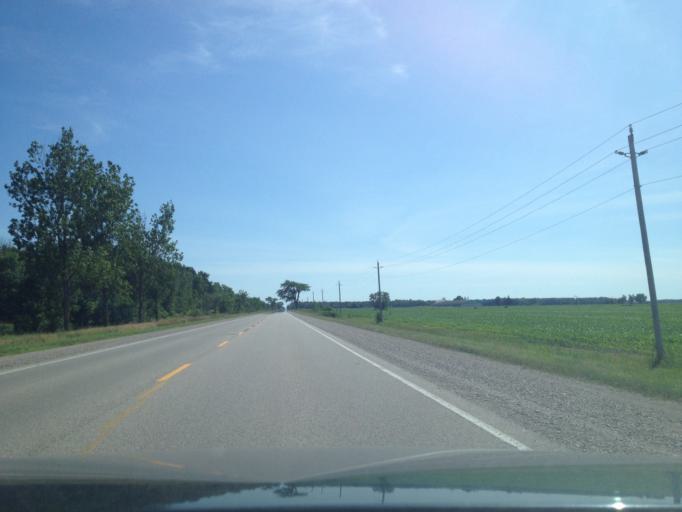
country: CA
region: Ontario
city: Stratford
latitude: 43.4778
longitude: -80.8962
